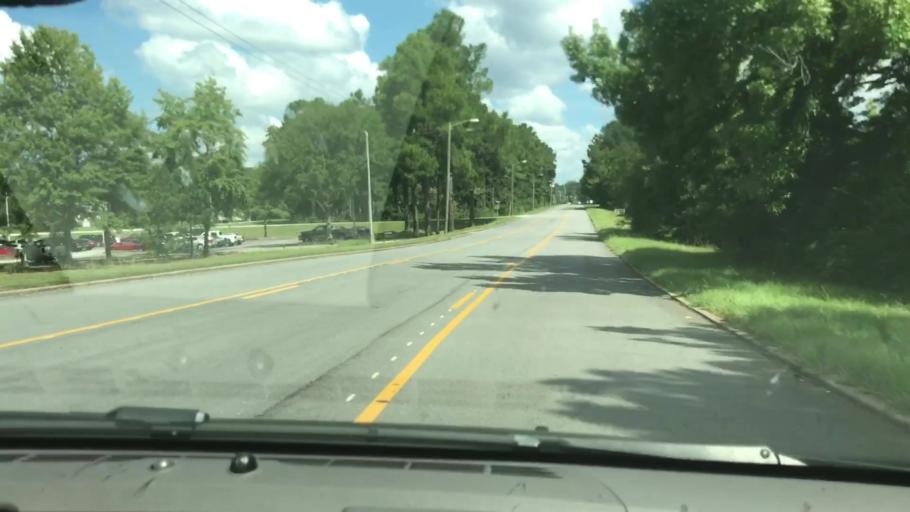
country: US
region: Georgia
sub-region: Troup County
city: La Grange
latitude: 33.0072
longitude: -85.0574
